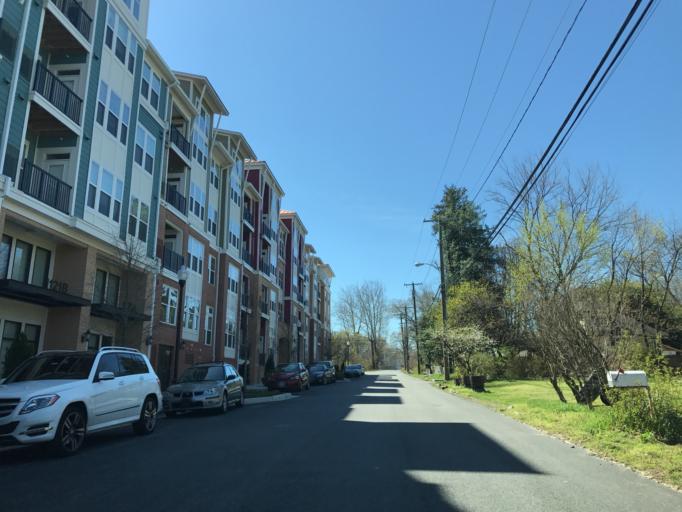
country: US
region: Maryland
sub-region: Anne Arundel County
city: Odenton
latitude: 39.0927
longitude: -76.7099
